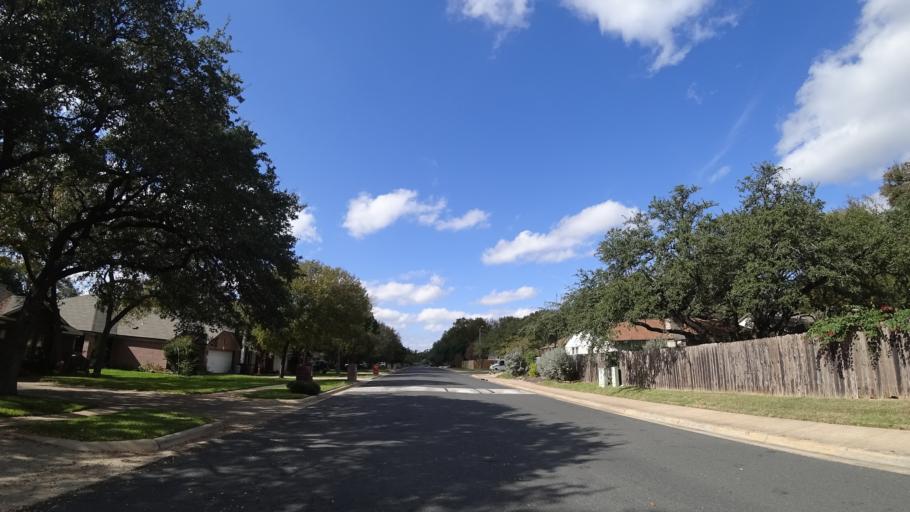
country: US
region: Texas
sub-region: Travis County
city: Wells Branch
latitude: 30.4137
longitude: -97.7261
